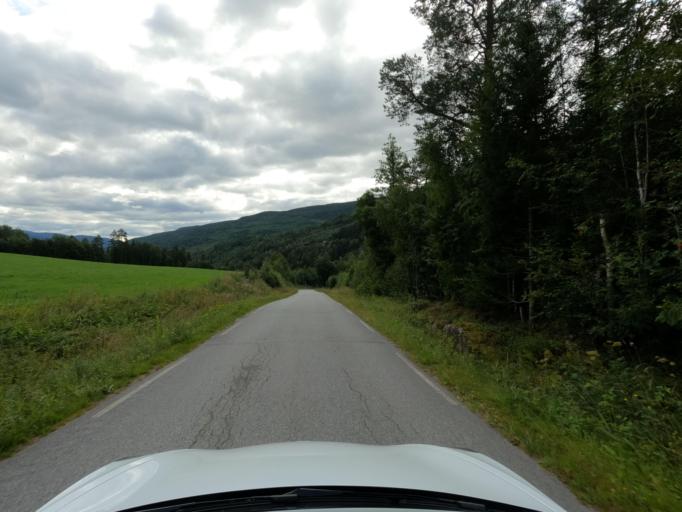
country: NO
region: Telemark
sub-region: Tinn
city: Rjukan
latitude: 59.9931
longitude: 8.6971
